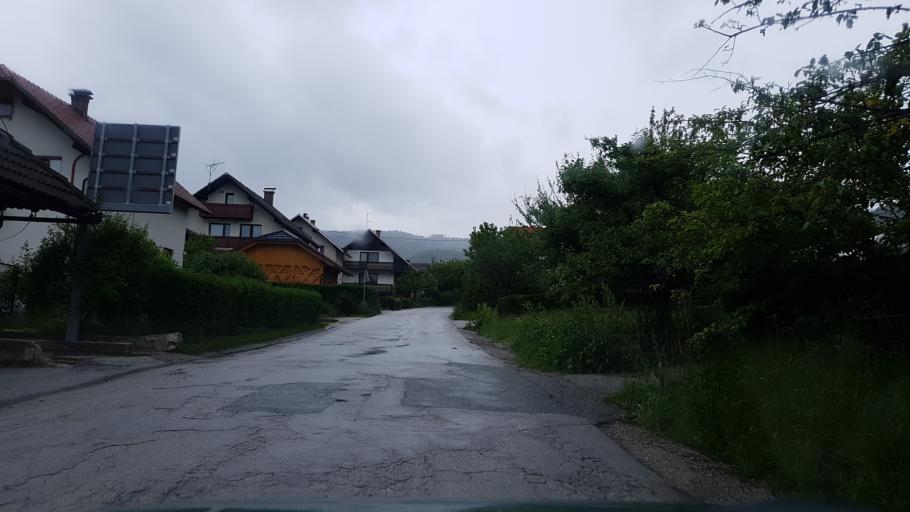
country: SI
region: Gorje
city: Zgornje Gorje
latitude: 46.3855
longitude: 14.0773
